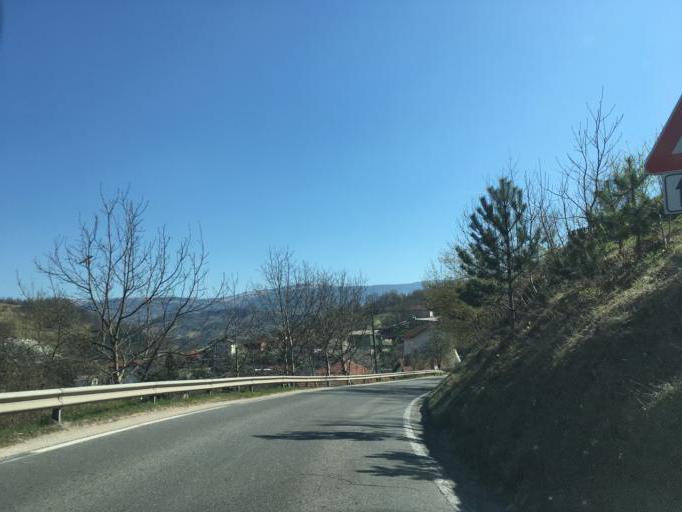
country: BA
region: Federation of Bosnia and Herzegovina
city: Jajce
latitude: 44.3394
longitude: 17.2752
